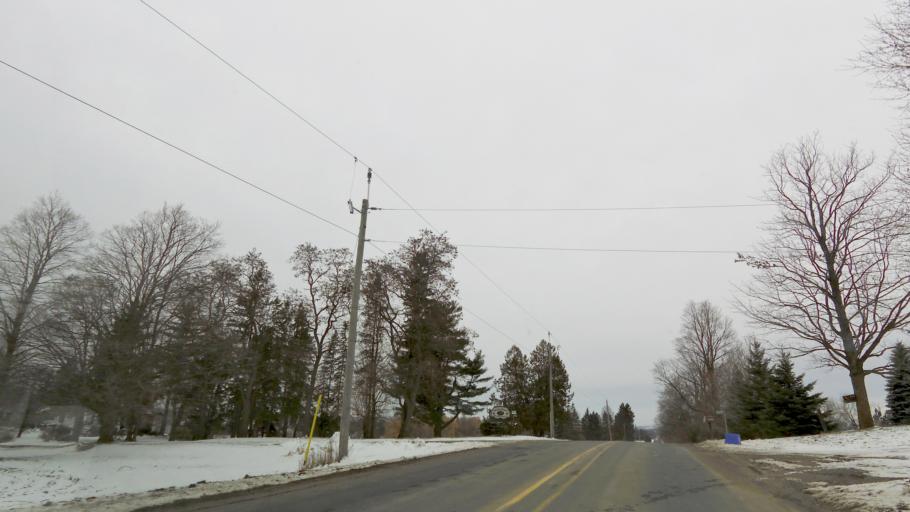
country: CA
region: Ontario
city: Bradford West Gwillimbury
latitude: 43.9672
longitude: -79.6426
